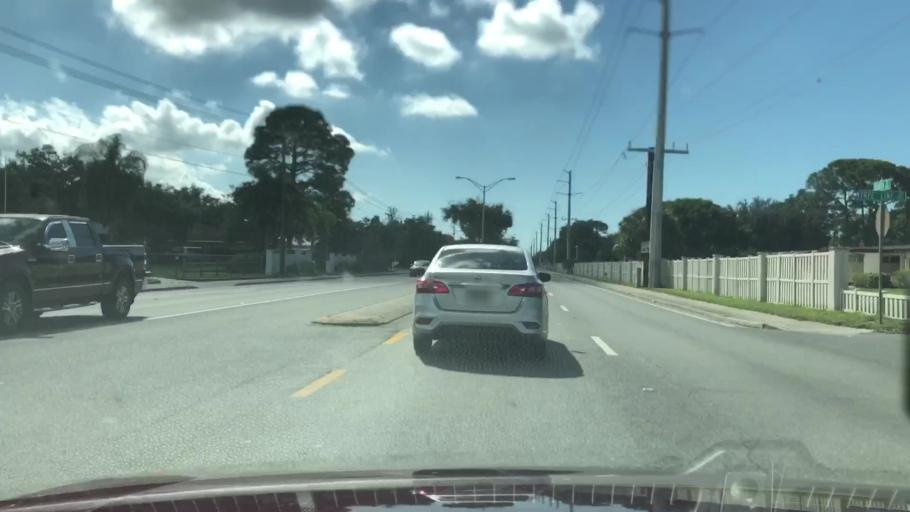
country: US
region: Florida
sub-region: Sarasota County
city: South Gate Ridge
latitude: 27.2657
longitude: -82.4977
